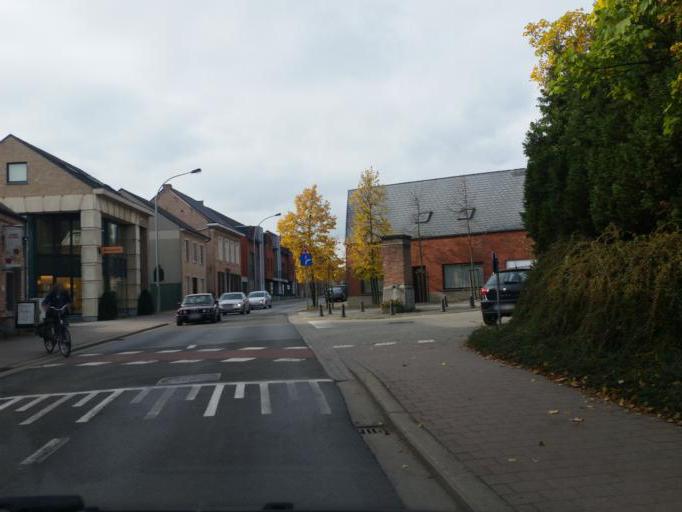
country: BE
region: Flanders
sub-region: Provincie Antwerpen
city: Heist-op-den-Berg
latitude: 51.0739
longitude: 4.7317
